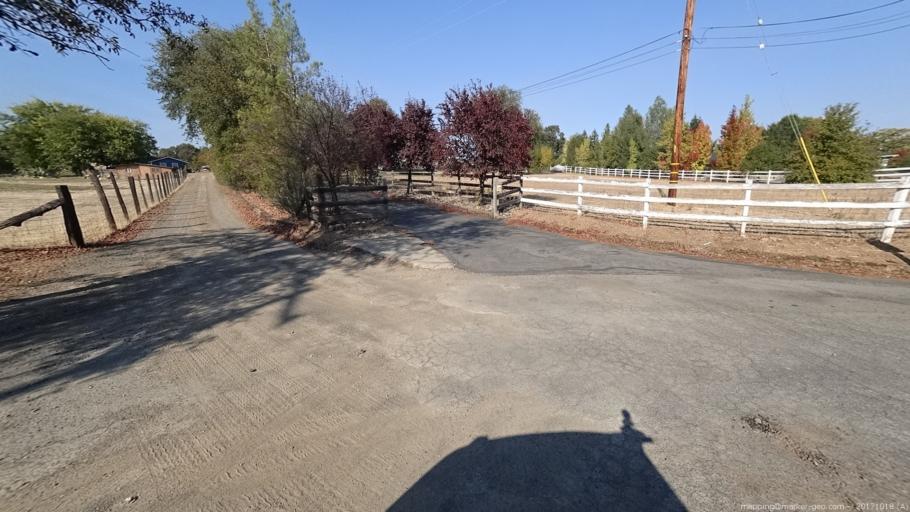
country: US
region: California
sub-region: Shasta County
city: Palo Cedro
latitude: 40.5770
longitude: -122.2319
